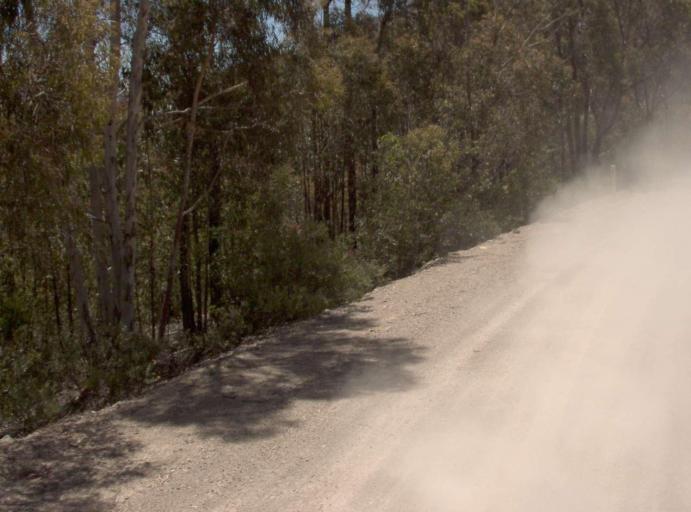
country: AU
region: New South Wales
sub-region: Snowy River
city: Jindabyne
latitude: -37.0766
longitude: 148.3278
